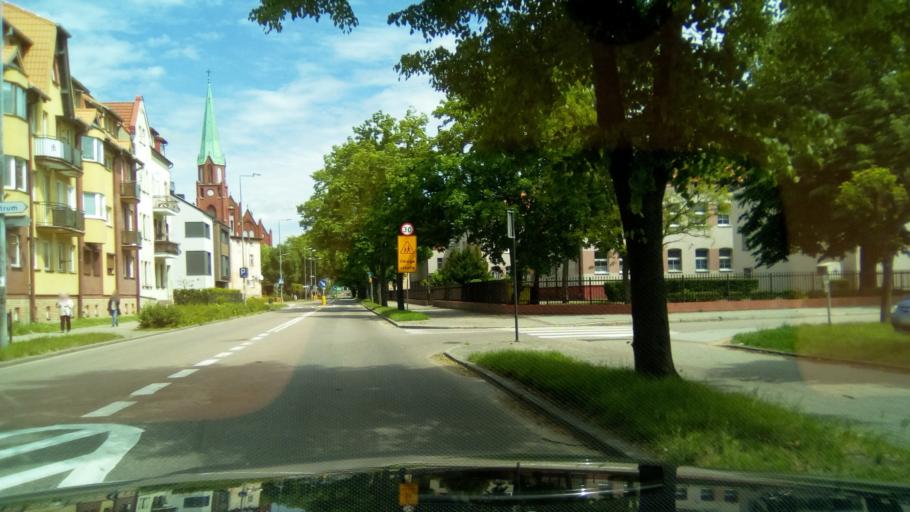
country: PL
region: Pomeranian Voivodeship
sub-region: Powiat leborski
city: Lebork
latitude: 54.5439
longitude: 17.7454
